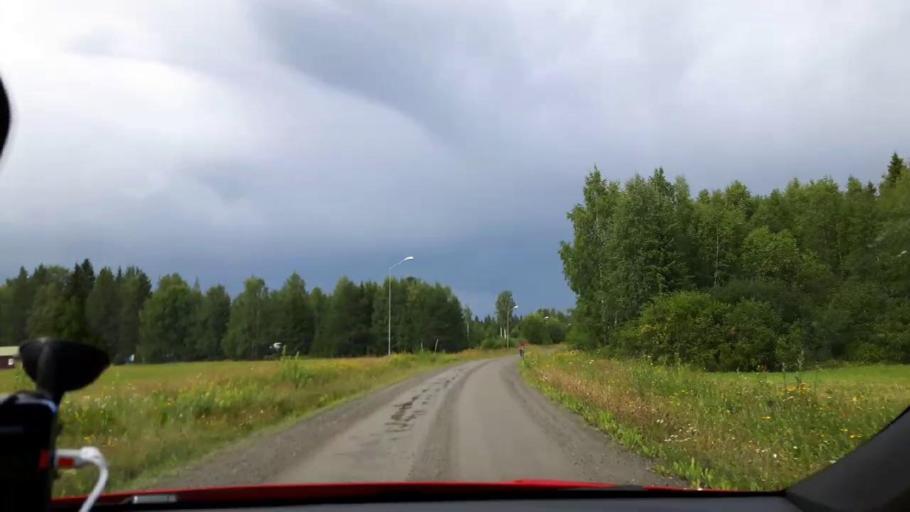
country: SE
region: Jaemtland
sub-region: Stroemsunds Kommun
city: Stroemsund
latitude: 64.0581
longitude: 15.8903
